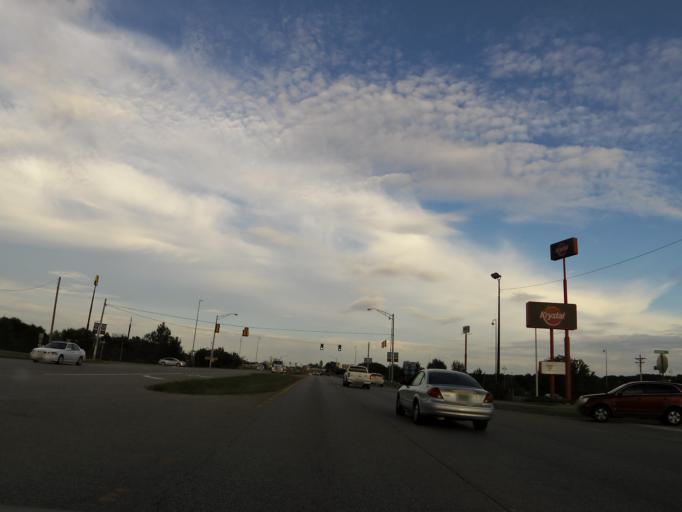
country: US
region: Alabama
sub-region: Limestone County
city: Athens
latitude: 34.7835
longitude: -86.9419
